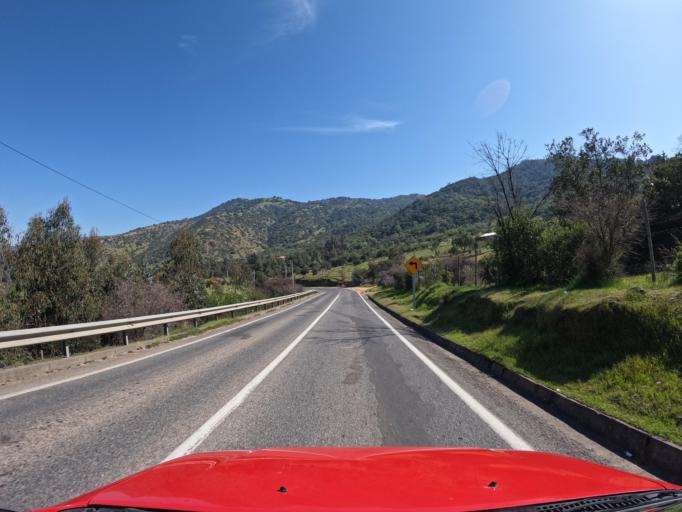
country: CL
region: Maule
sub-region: Provincia de Curico
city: Rauco
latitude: -35.0488
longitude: -71.5964
